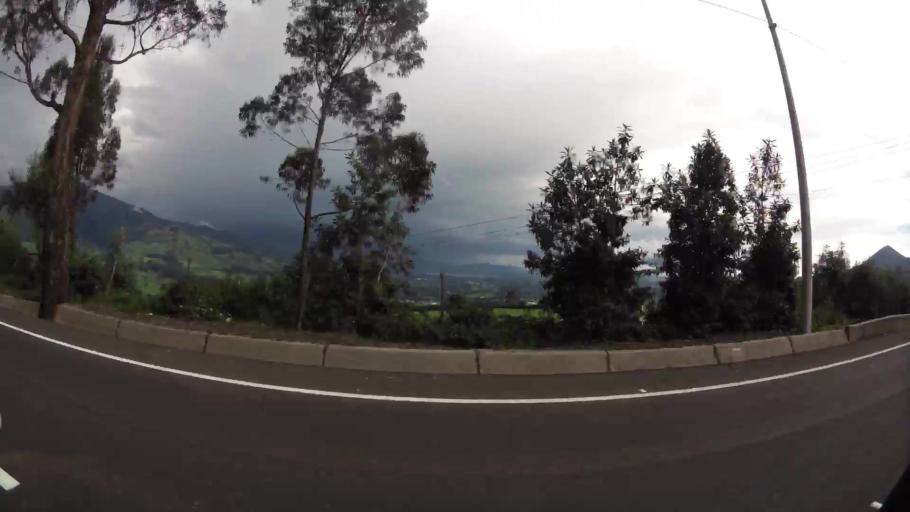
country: EC
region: Pichincha
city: Sangolqui
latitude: -0.3910
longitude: -78.5442
